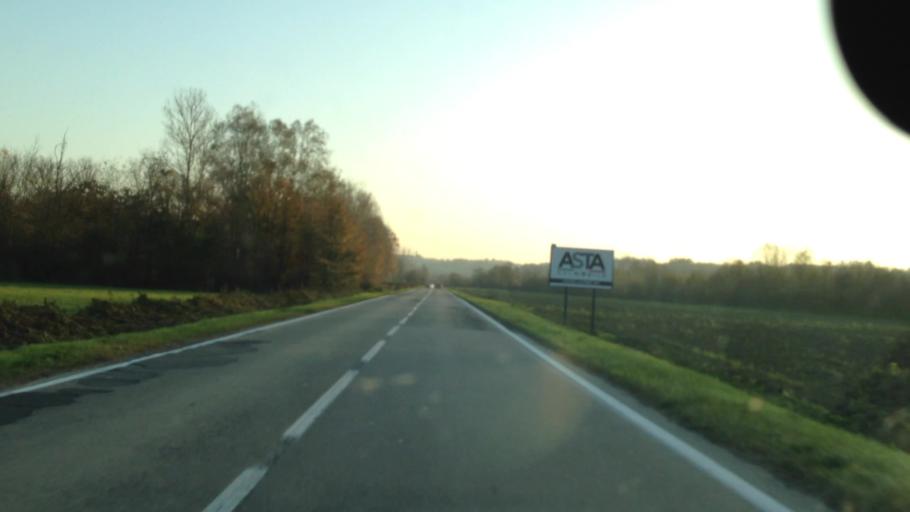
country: IT
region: Piedmont
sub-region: Provincia di Asti
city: Montiglio
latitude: 45.0509
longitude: 8.1123
